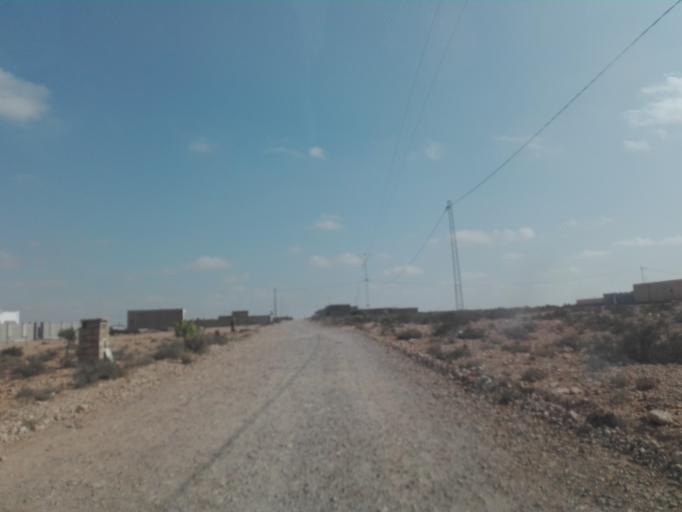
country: TN
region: Madanin
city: Medenine
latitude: 33.4294
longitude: 10.4065
